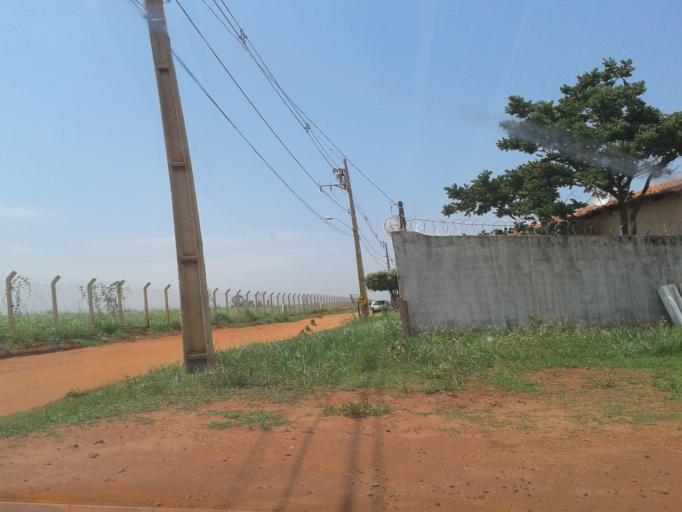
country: BR
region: Minas Gerais
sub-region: Ituiutaba
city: Ituiutaba
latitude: -18.9901
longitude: -49.4336
